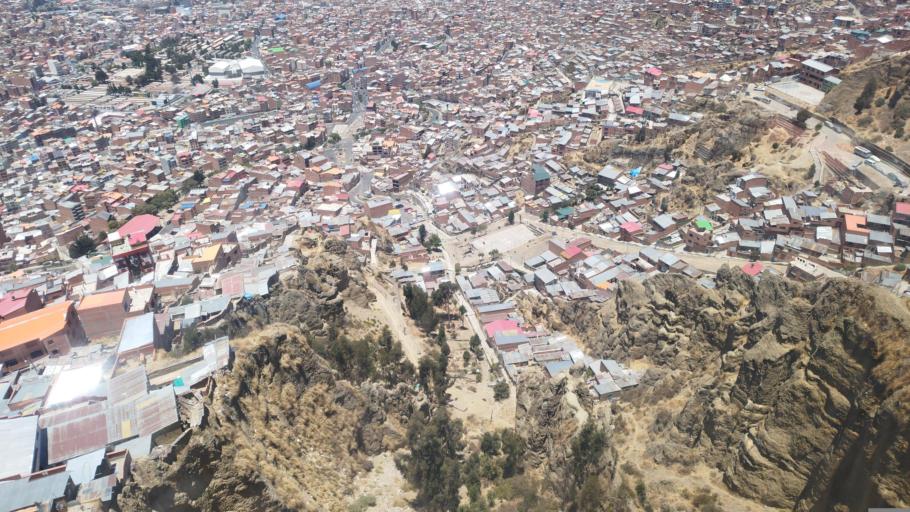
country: BO
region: La Paz
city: La Paz
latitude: -16.5029
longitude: -68.1612
